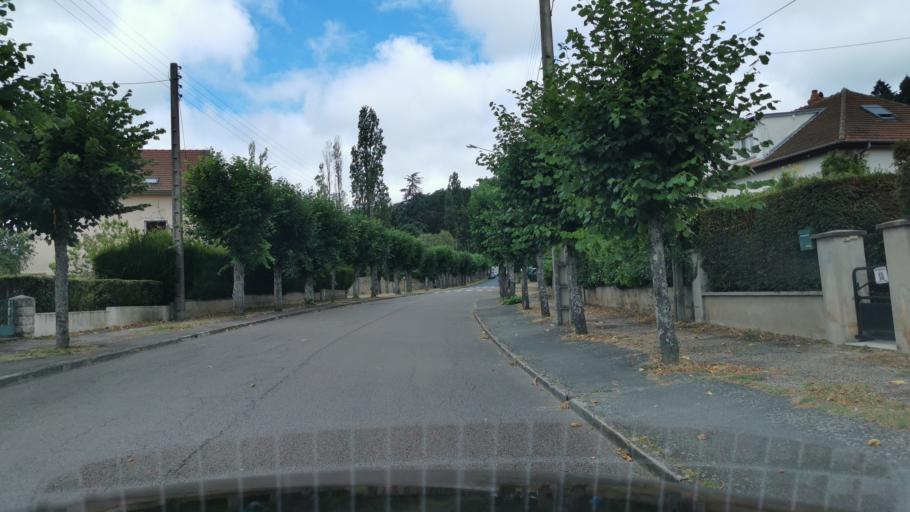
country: FR
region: Bourgogne
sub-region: Departement de Saone-et-Loire
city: Le Breuil
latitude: 46.8083
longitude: 4.4460
